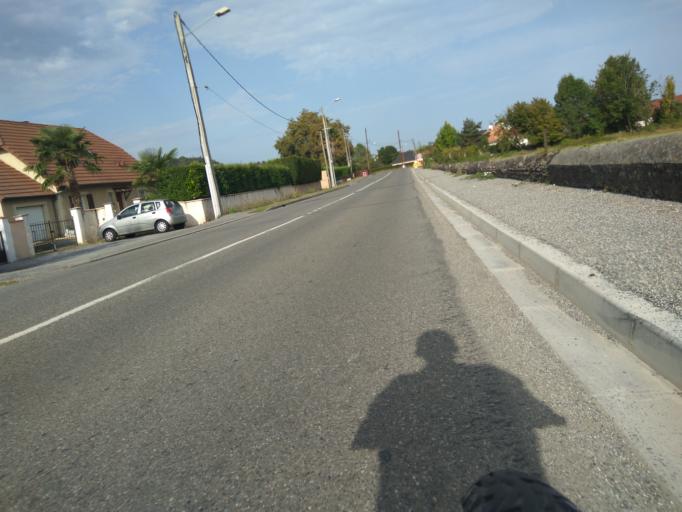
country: FR
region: Aquitaine
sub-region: Departement des Pyrenees-Atlantiques
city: Mazeres-Lezons
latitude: 43.2741
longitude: -0.3474
